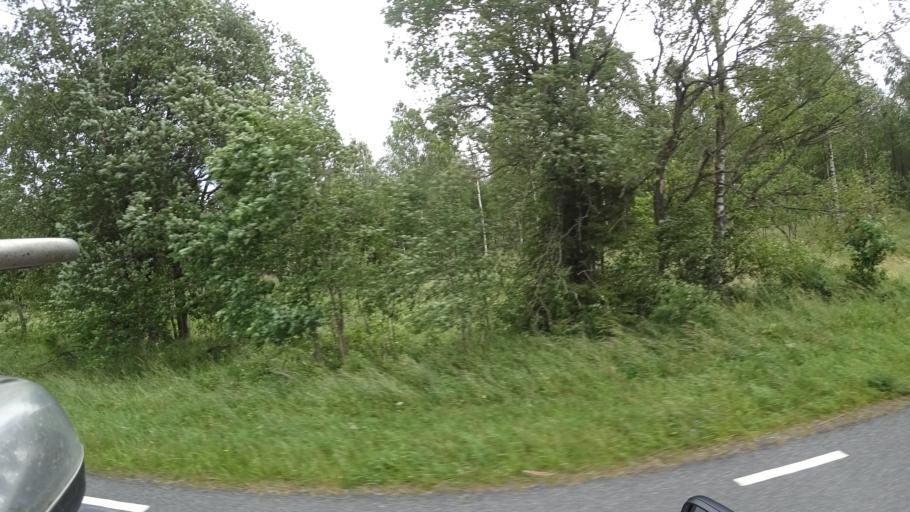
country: SE
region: Skane
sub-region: Kristianstads Kommun
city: Degeberga
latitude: 55.7193
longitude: 13.9921
